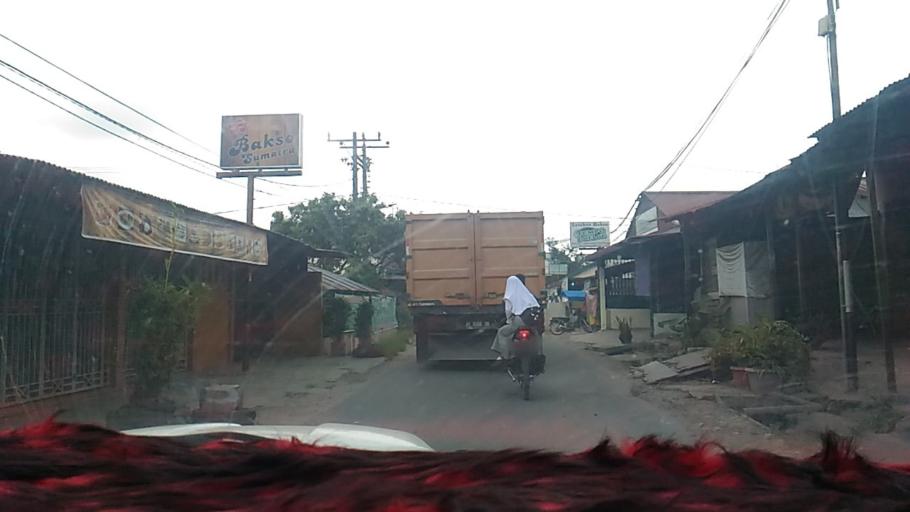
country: ID
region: North Sumatra
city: Binjai
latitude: 3.5969
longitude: 98.5515
